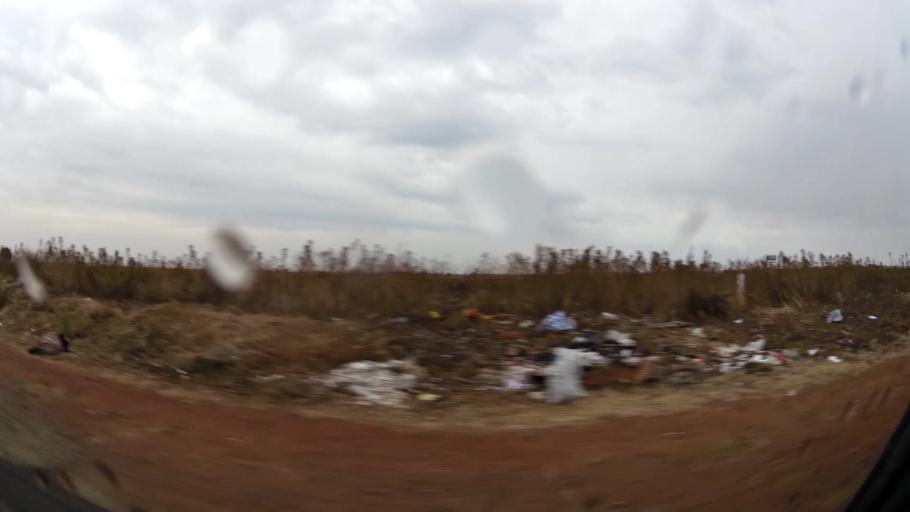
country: ZA
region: Gauteng
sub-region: City of Johannesburg Metropolitan Municipality
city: Roodepoort
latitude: -26.1737
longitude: 27.8029
